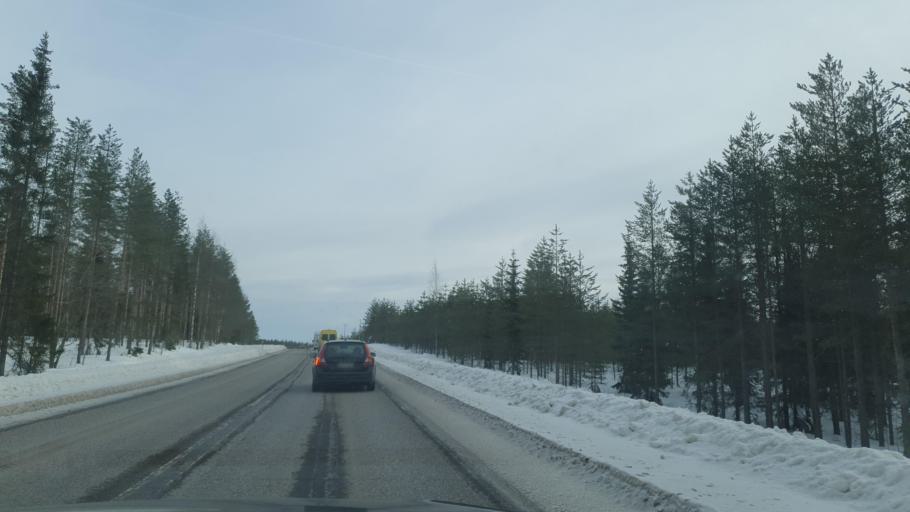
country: FI
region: Kainuu
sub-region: Kajaani
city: Kajaani
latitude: 64.4507
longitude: 27.5062
